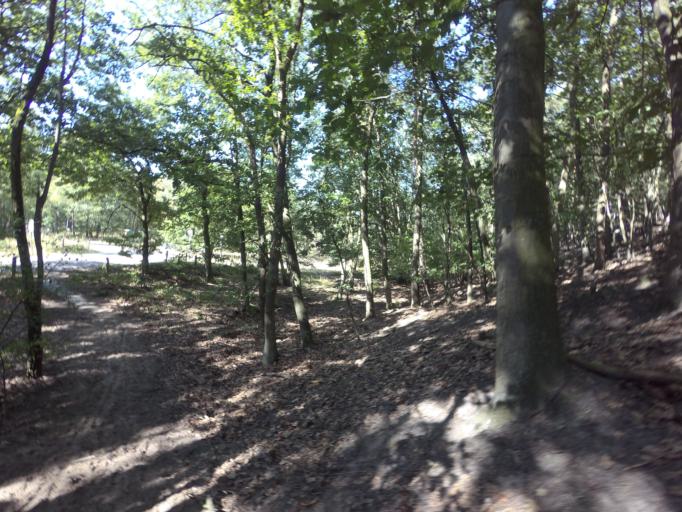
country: DE
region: North Rhine-Westphalia
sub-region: Regierungsbezirk Koln
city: Wassenberg
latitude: 51.1533
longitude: 6.1582
